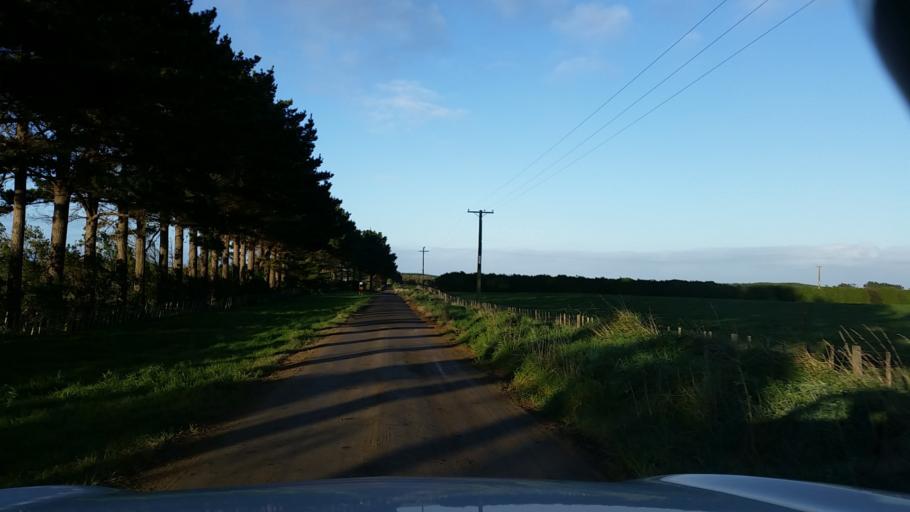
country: NZ
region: Manawatu-Wanganui
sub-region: Wanganui District
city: Wanganui
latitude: -39.8235
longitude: 174.7982
